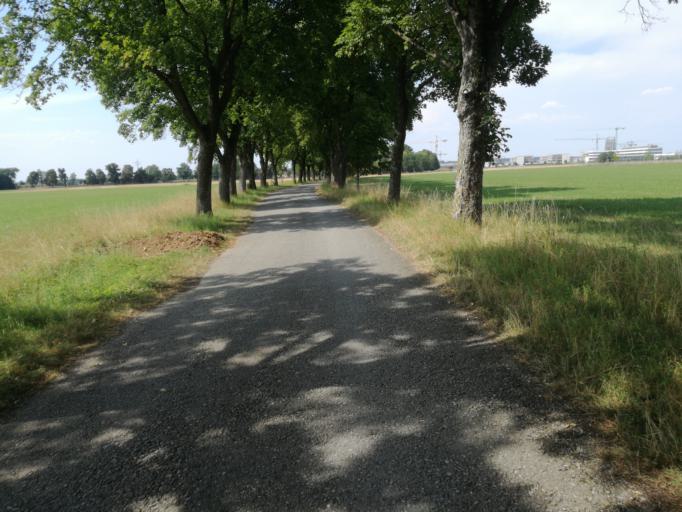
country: DE
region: Bavaria
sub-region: Upper Bavaria
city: Grafelfing
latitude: 48.1315
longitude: 11.4067
